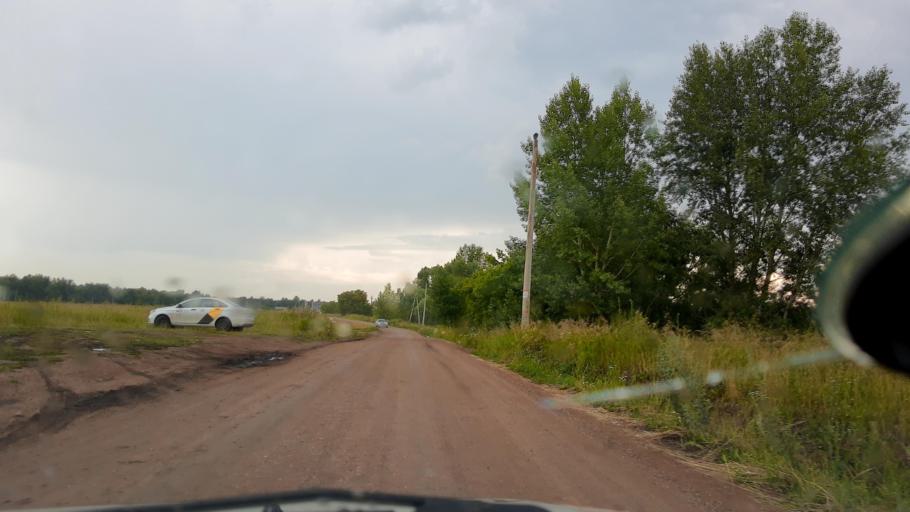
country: RU
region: Bashkortostan
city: Mikhaylovka
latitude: 54.7112
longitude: 55.8680
